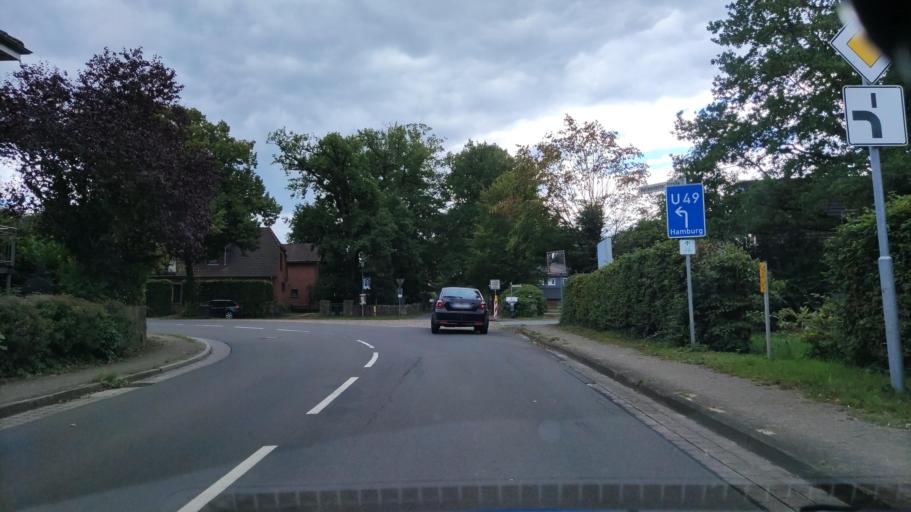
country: DE
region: Lower Saxony
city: Dohren
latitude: 53.3033
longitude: 9.7029
